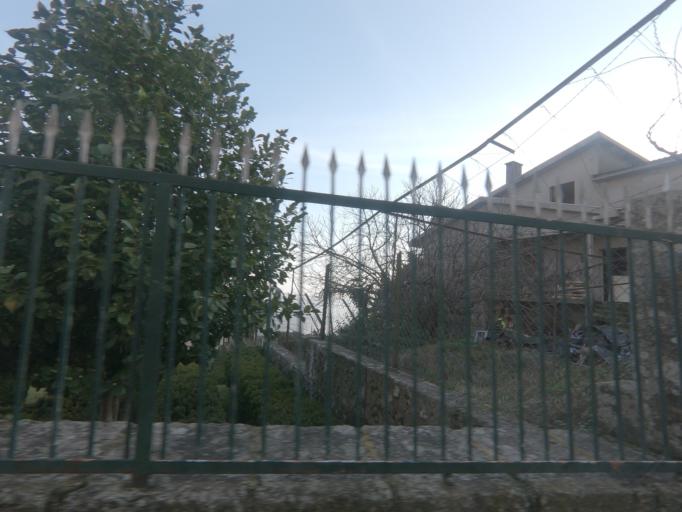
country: PT
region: Vila Real
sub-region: Vila Real
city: Vila Real
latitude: 41.3214
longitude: -7.7827
